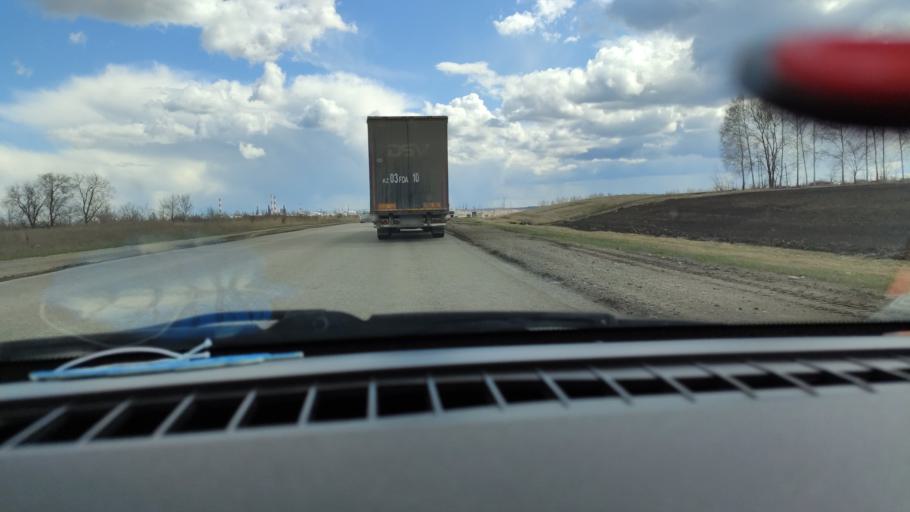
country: RU
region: Samara
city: Varlamovo
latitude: 53.1089
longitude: 48.3555
